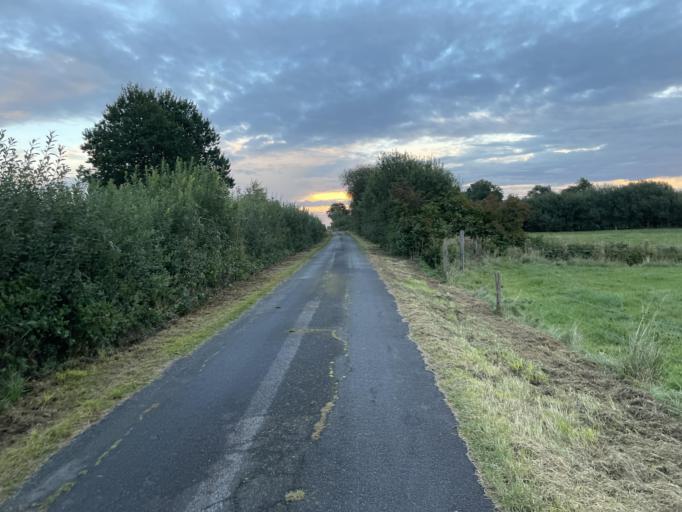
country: DE
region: Schleswig-Holstein
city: Schwesing
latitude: 54.4777
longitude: 9.1243
